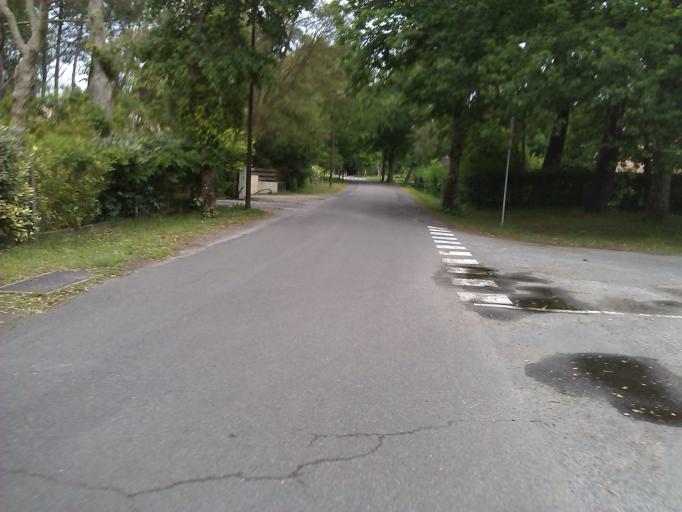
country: FR
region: Aquitaine
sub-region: Departement des Landes
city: Leon
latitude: 43.8476
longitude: -1.3546
